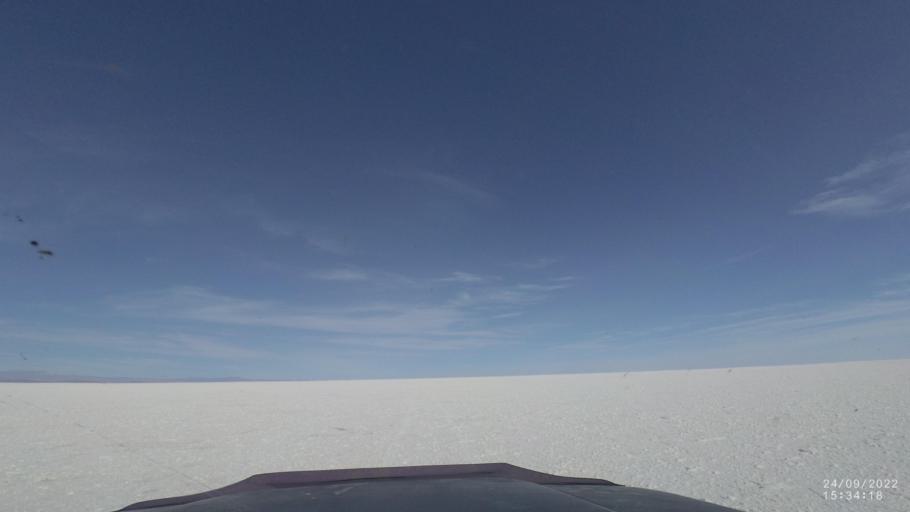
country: BO
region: Potosi
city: Colchani
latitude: -20.1232
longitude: -67.2636
